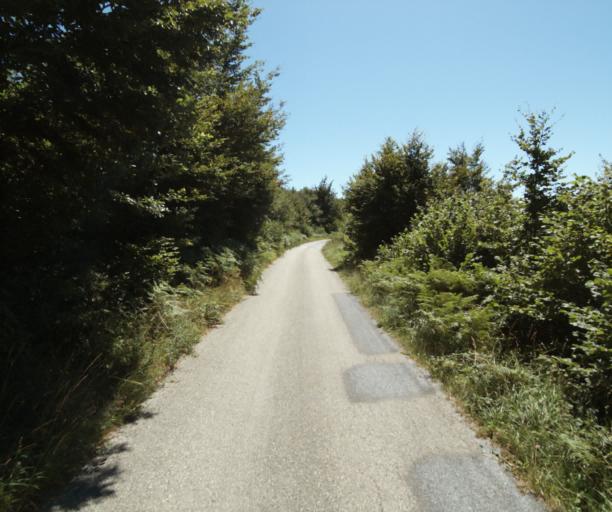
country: FR
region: Languedoc-Roussillon
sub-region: Departement de l'Aude
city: Cuxac-Cabardes
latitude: 43.4078
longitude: 2.2008
